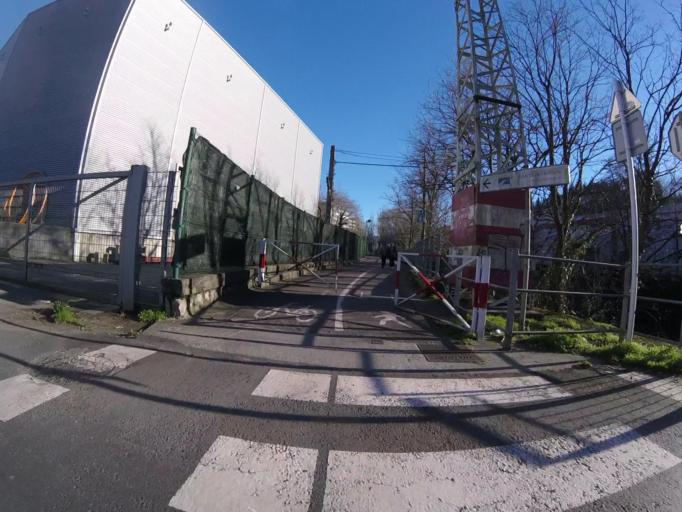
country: ES
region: Basque Country
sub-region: Provincia de Guipuzcoa
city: Errenteria
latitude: 43.3033
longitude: -1.8850
